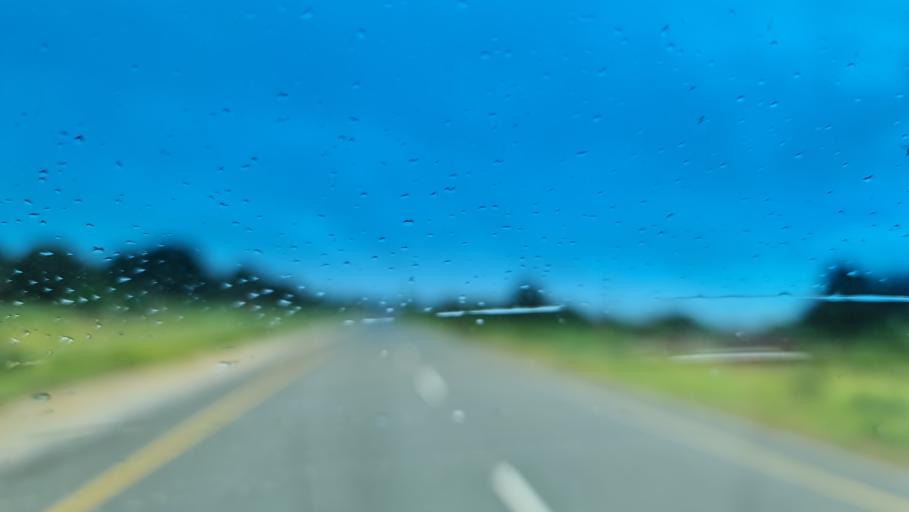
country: MZ
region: Nampula
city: Nampula
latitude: -15.5078
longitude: 39.3333
